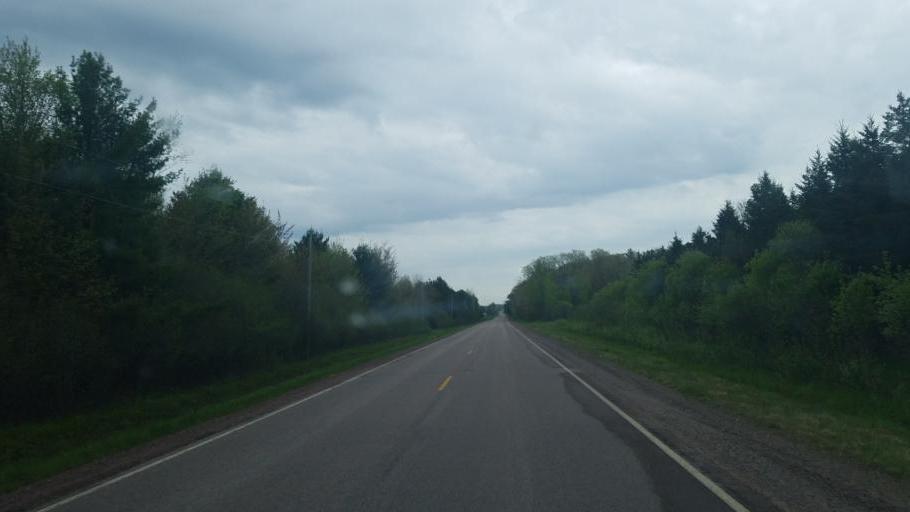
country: US
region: Wisconsin
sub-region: Wood County
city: Marshfield
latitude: 44.5612
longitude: -90.3000
